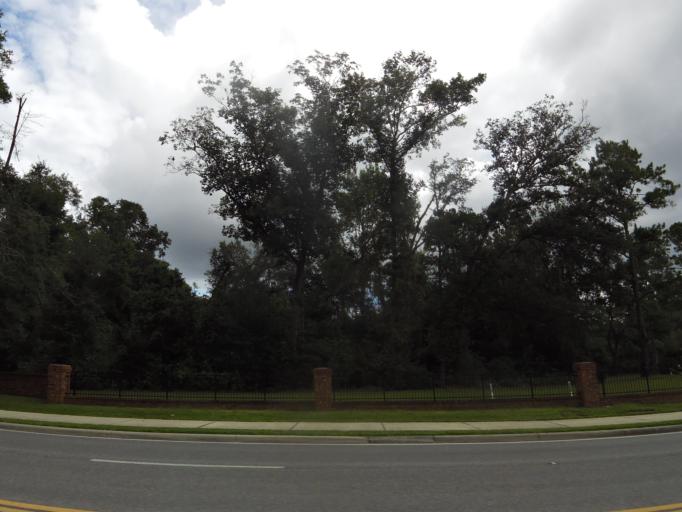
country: US
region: Florida
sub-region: Clay County
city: Asbury Lake
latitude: 30.0912
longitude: -81.8098
